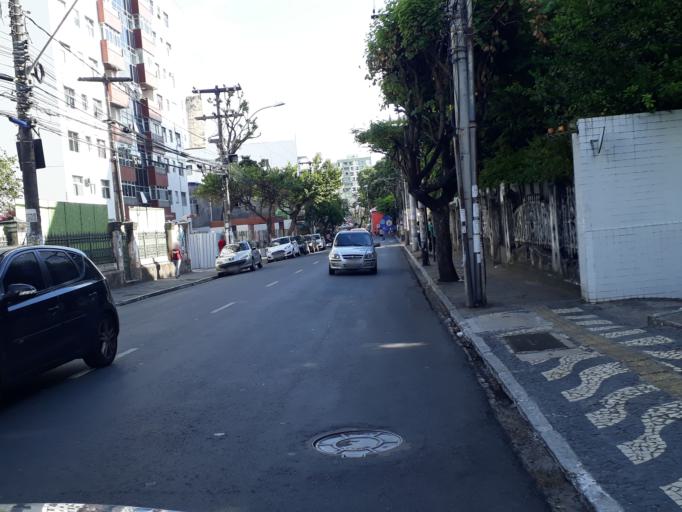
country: BR
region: Bahia
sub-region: Salvador
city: Salvador
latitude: -12.9915
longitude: -38.5212
